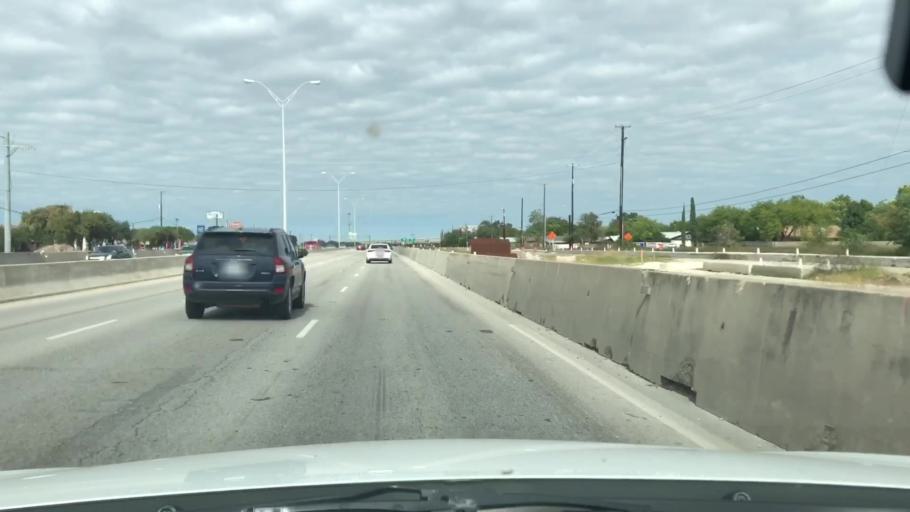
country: US
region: Texas
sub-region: Bexar County
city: Lackland Air Force Base
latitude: 29.4217
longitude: -98.6495
